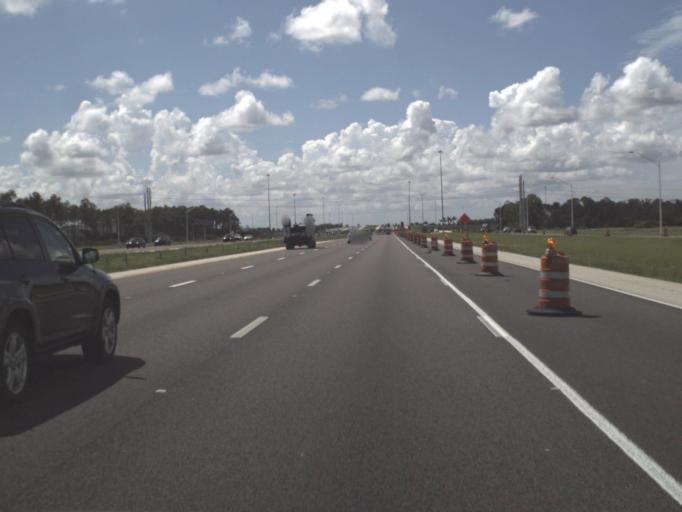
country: US
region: Florida
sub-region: Lee County
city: Three Oaks
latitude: 26.5045
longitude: -81.7947
